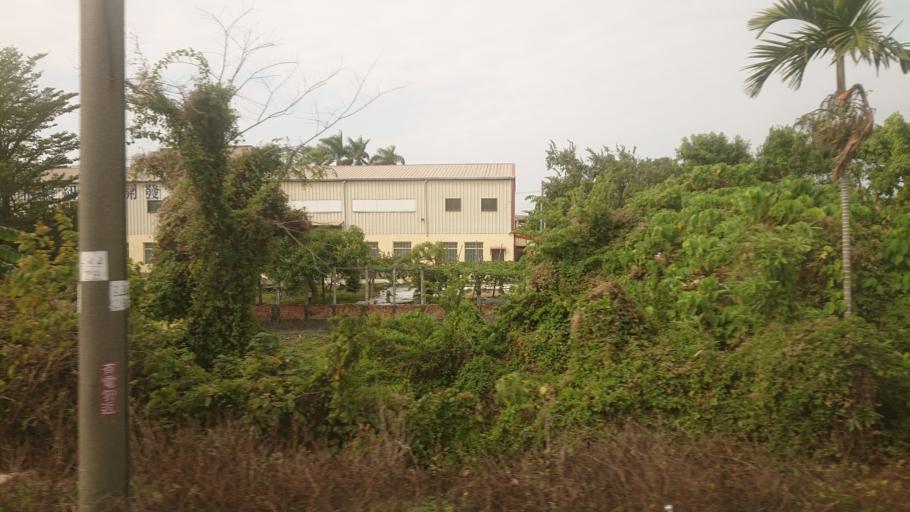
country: TW
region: Taiwan
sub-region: Changhua
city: Chang-hua
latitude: 24.0233
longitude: 120.5377
